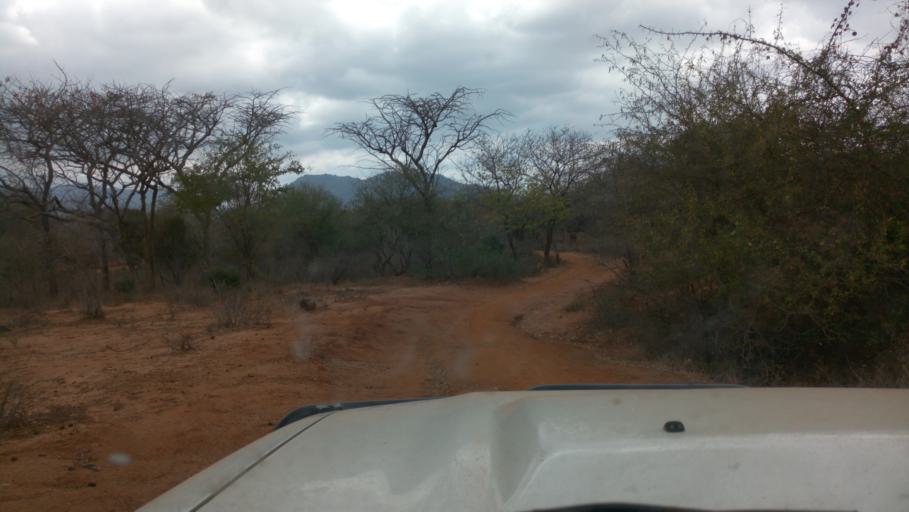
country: KE
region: Kitui
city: Kitui
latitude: -1.8555
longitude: 38.3588
